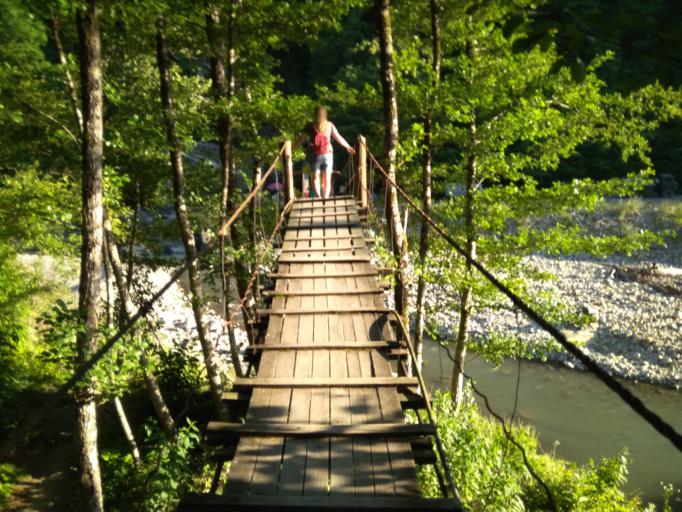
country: RU
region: Krasnodarskiy
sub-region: Sochi City
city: Lazarevskoye
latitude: 43.9996
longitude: 39.3970
